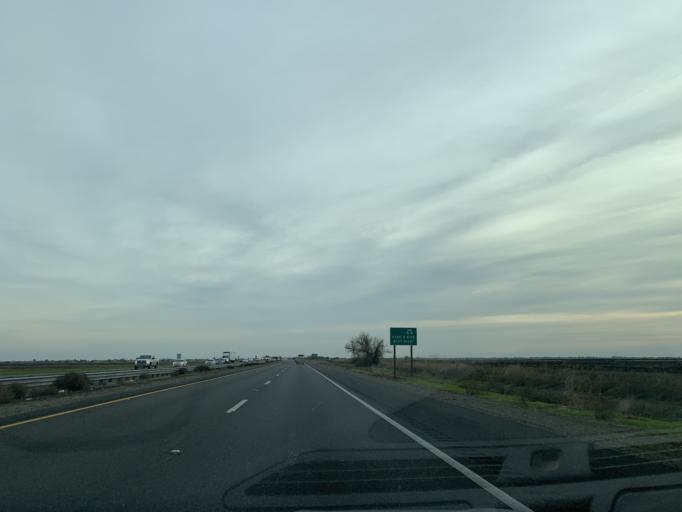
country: US
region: California
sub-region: Sacramento County
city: Elverta
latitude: 38.6991
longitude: -121.5404
